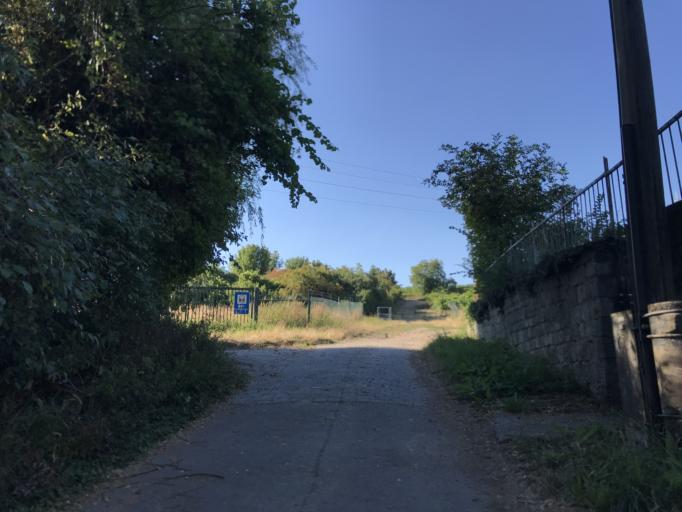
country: DE
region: Rheinland-Pfalz
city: Stadecken-Elsheim
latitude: 49.9235
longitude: 8.1242
